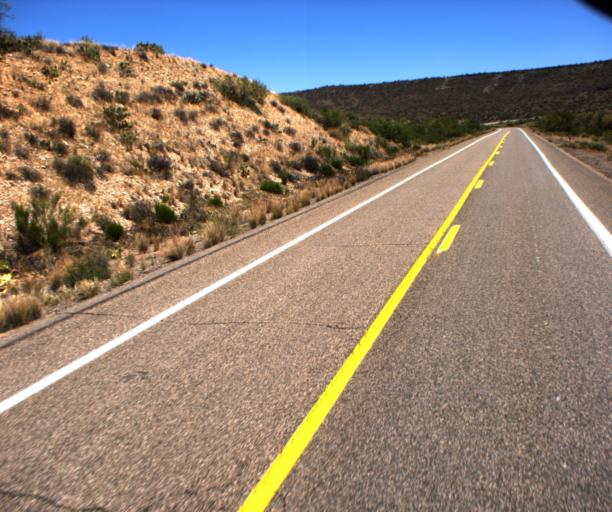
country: US
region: Arizona
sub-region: Yavapai County
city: Bagdad
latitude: 34.5164
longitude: -113.0856
